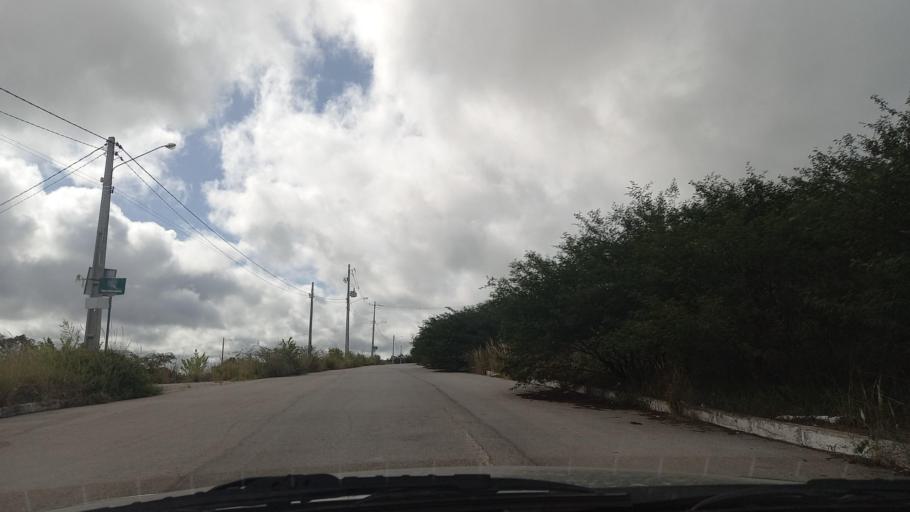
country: BR
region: Pernambuco
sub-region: Caruaru
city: Caruaru
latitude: -8.3068
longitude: -35.9591
